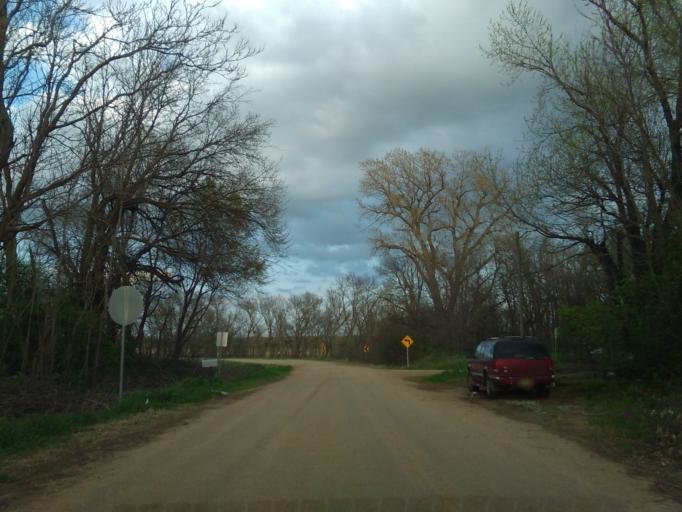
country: US
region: Nebraska
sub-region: Webster County
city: Red Cloud
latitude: 40.1715
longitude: -98.4456
